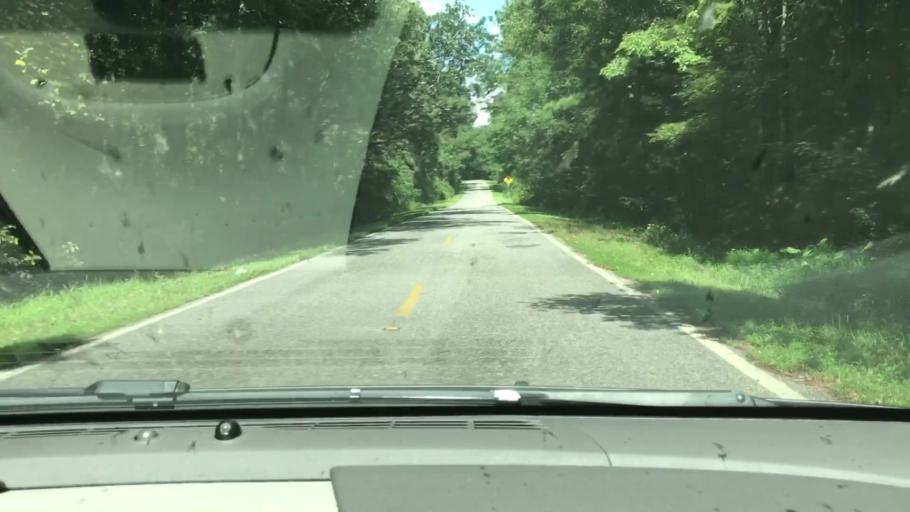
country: US
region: Georgia
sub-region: Quitman County
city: Georgetown
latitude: 31.7491
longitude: -85.0770
